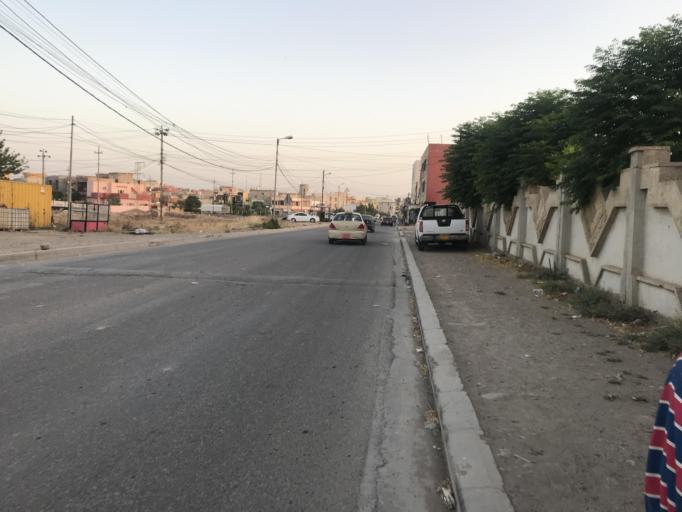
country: IQ
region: Dahuk
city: Saymayl
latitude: 36.8595
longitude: 42.8359
